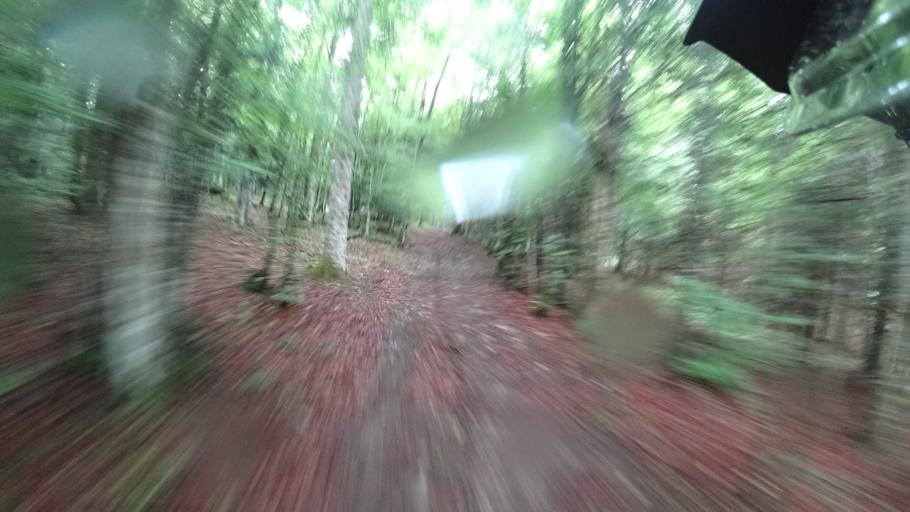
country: HR
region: Primorsko-Goranska
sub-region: Grad Delnice
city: Delnice
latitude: 45.3607
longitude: 14.8922
